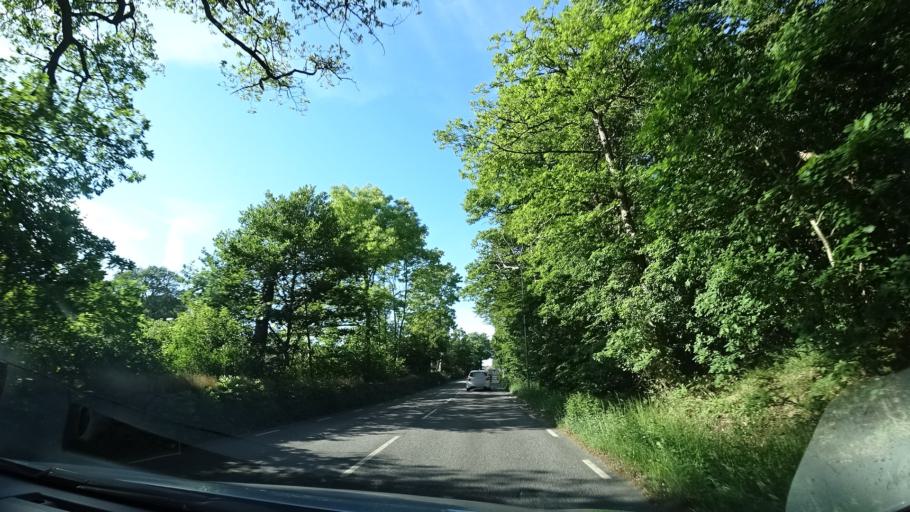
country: SE
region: Vaestra Goetaland
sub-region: Goteborg
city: Billdal
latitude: 57.5844
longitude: 11.9394
